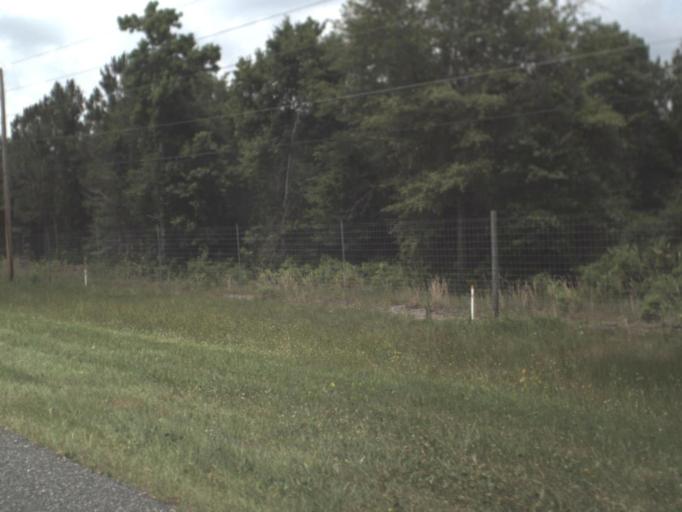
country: US
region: Florida
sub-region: Clay County
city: Green Cove Springs
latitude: 29.8349
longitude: -81.6616
